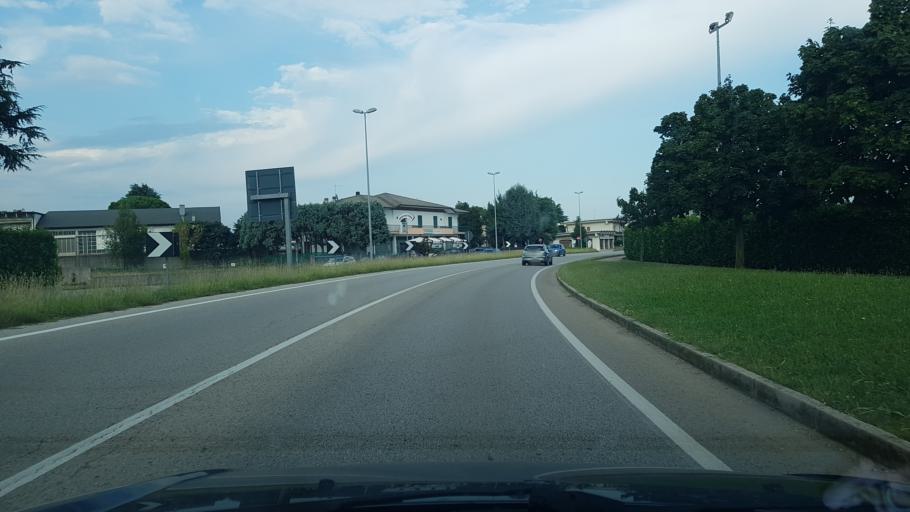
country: IT
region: Veneto
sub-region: Provincia di Vicenza
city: Marano Vicentino
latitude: 45.6994
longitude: 11.4331
